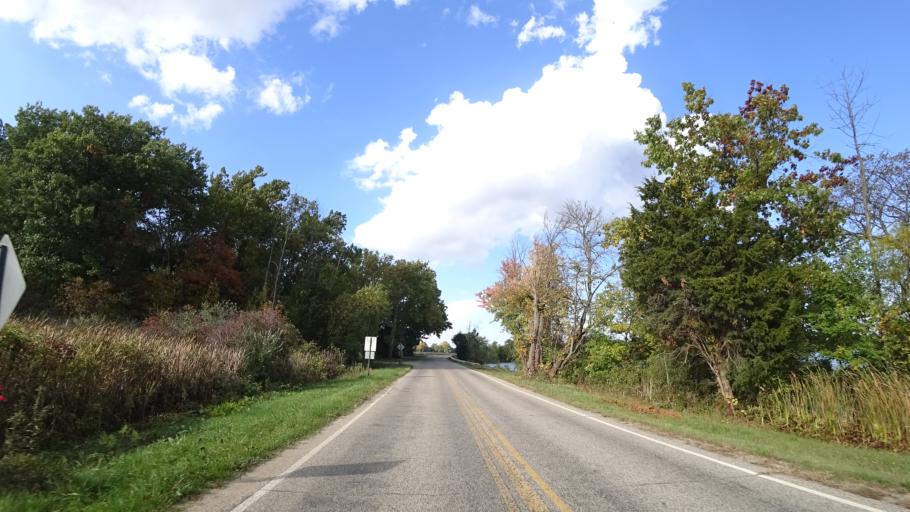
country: US
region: Michigan
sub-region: Saint Joseph County
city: Centreville
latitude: 41.9702
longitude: -85.5300
